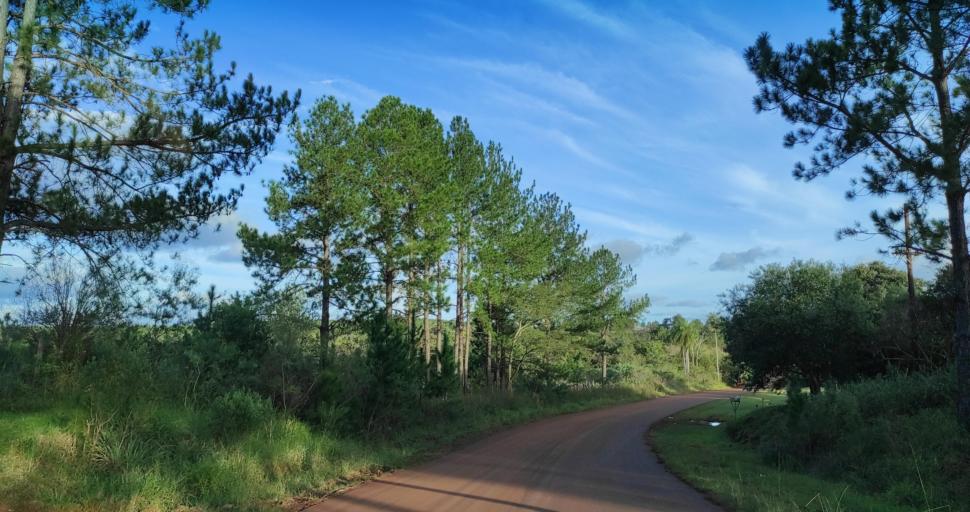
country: AR
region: Misiones
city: Garupa
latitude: -27.5080
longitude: -55.8548
